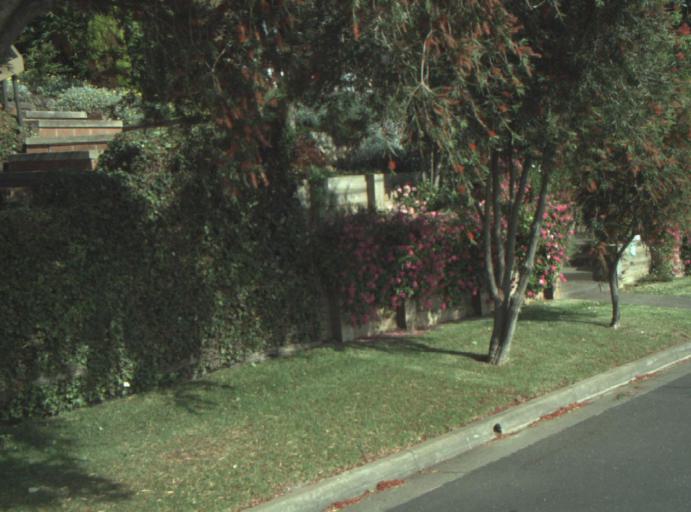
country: AU
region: Victoria
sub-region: Greater Geelong
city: Wandana Heights
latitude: -38.1589
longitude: 144.3201
